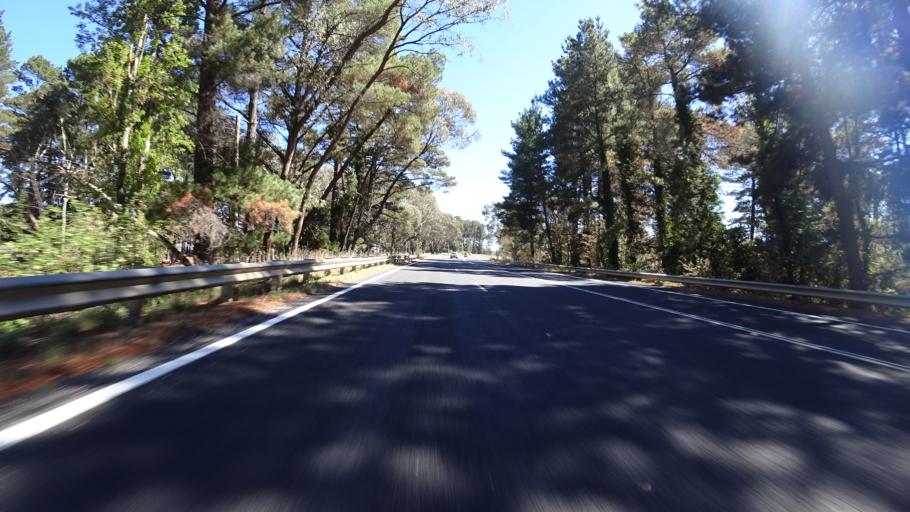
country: AU
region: New South Wales
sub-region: Lithgow
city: Portland
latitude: -33.3759
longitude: 150.0735
